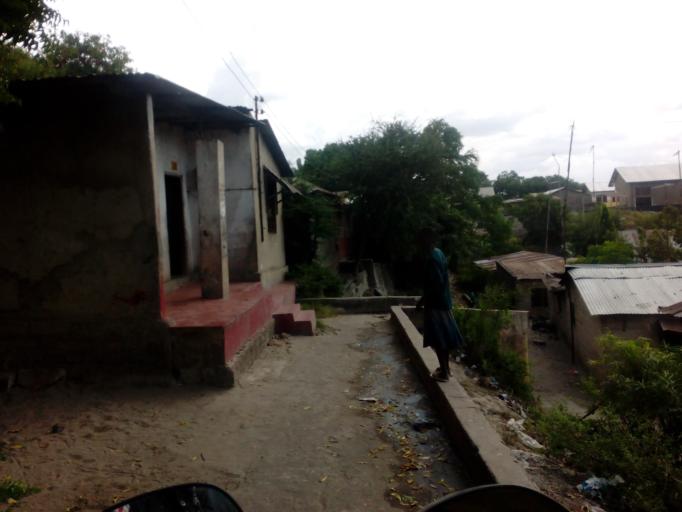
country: TZ
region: Dar es Salaam
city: Dar es Salaam
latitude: -6.8362
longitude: 39.2725
